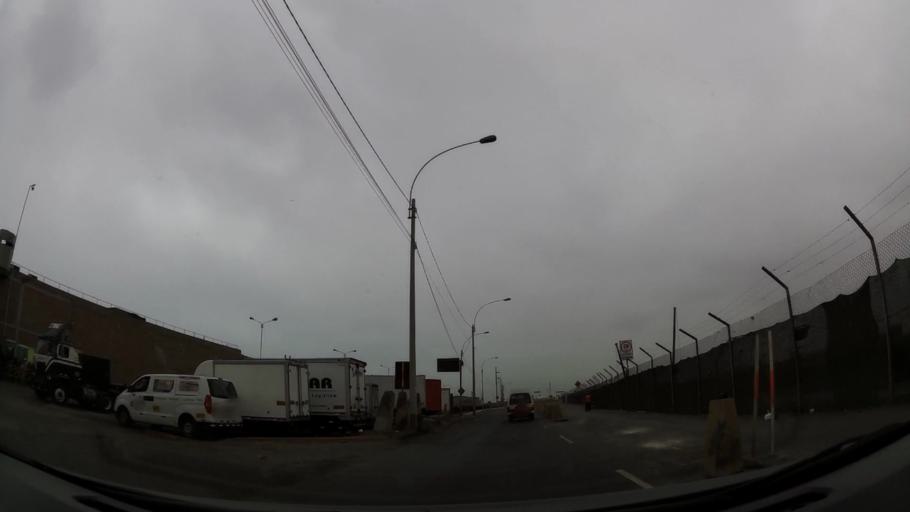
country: PE
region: Callao
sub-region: Callao
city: Callao
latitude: -12.0221
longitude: -77.1295
